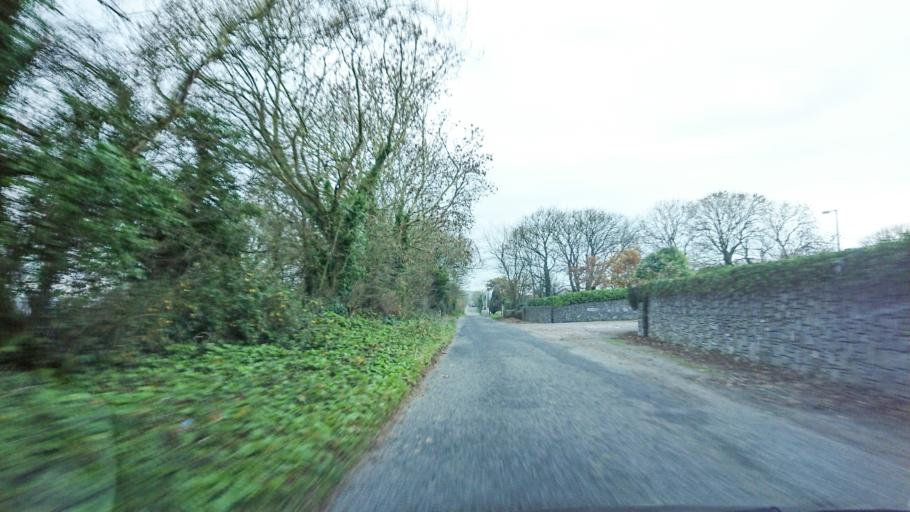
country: IE
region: Munster
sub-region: Waterford
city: Dunmore East
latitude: 52.2341
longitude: -6.9769
